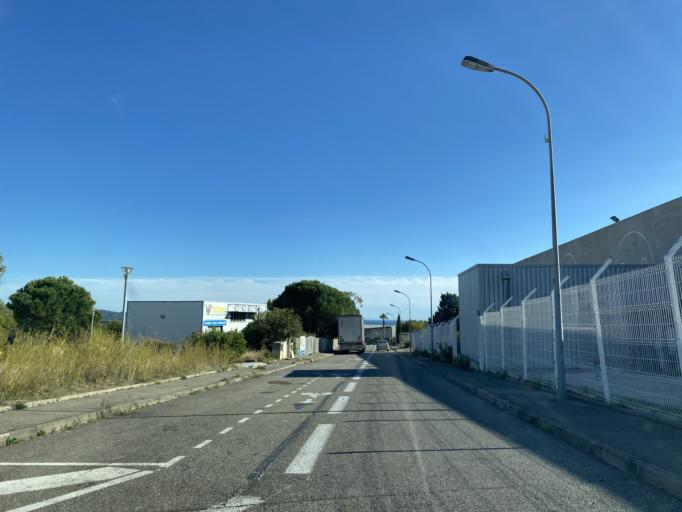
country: FR
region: Provence-Alpes-Cote d'Azur
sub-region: Departement des Bouches-du-Rhone
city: Ceyreste
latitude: 43.2075
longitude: 5.6064
